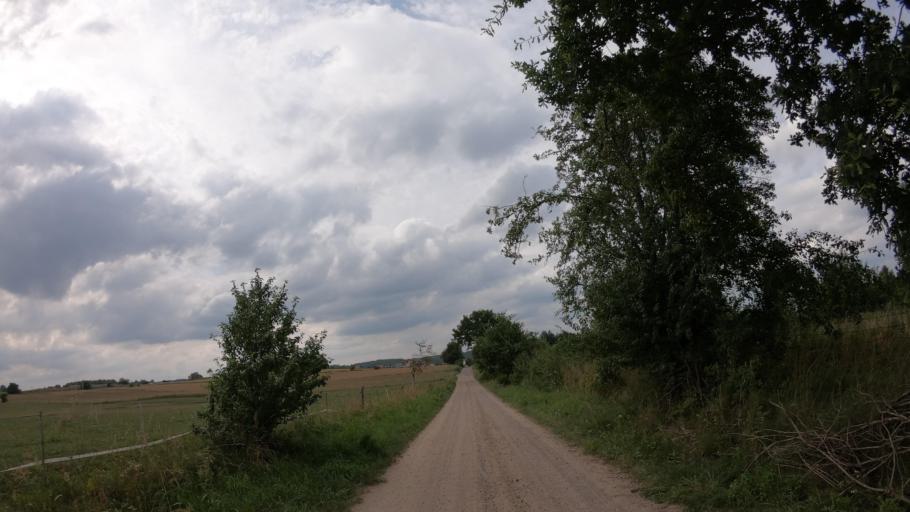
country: PL
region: West Pomeranian Voivodeship
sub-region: Powiat drawski
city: Kalisz Pomorski
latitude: 53.2939
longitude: 15.9246
